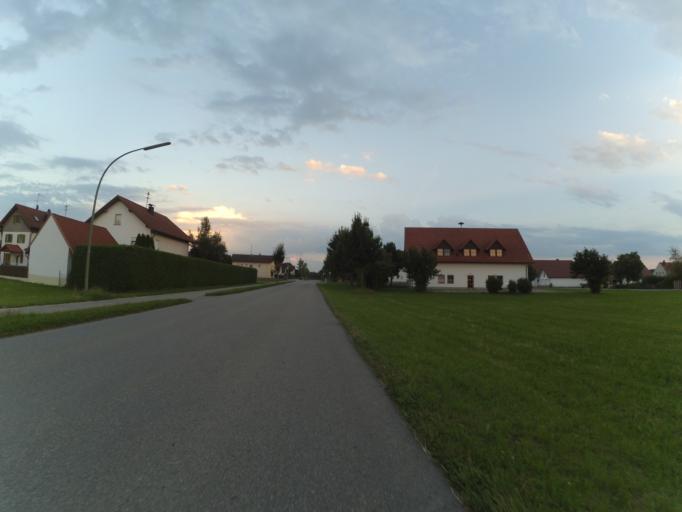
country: DE
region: Bavaria
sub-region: Swabia
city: Tussenhausen
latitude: 48.0627
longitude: 10.5832
